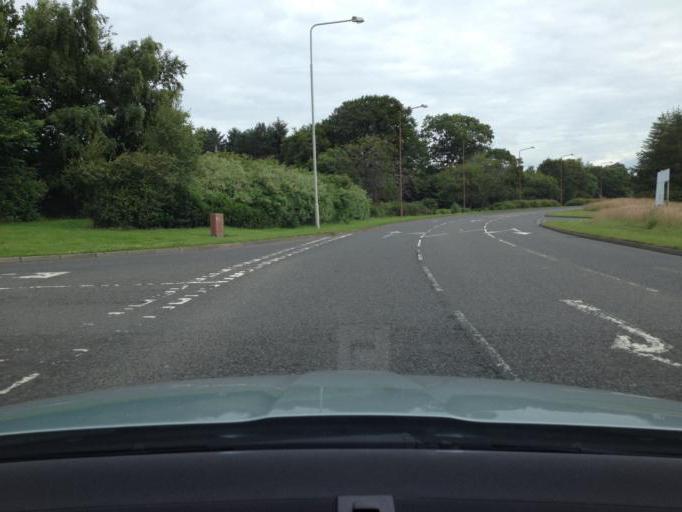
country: GB
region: Scotland
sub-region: West Lothian
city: Livingston
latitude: 55.8766
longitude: -3.5425
